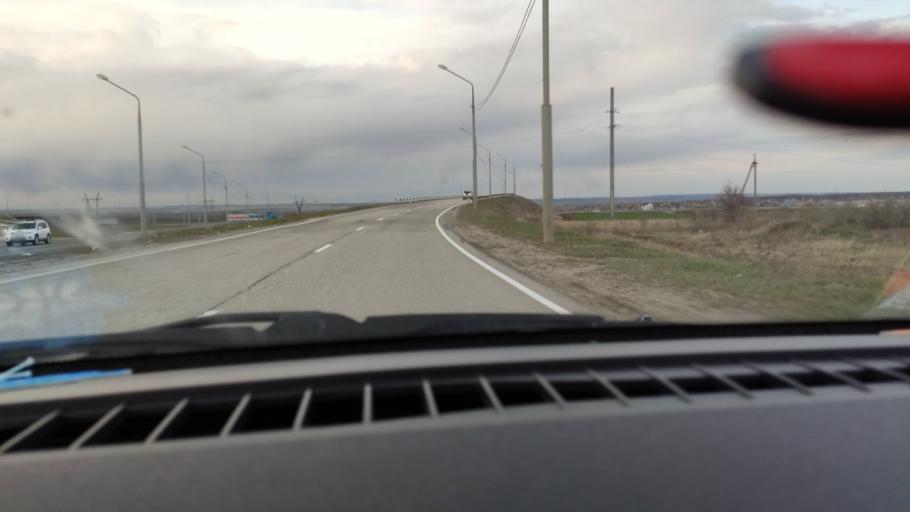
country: RU
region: Saratov
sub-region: Saratovskiy Rayon
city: Saratov
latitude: 51.6701
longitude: 46.0013
